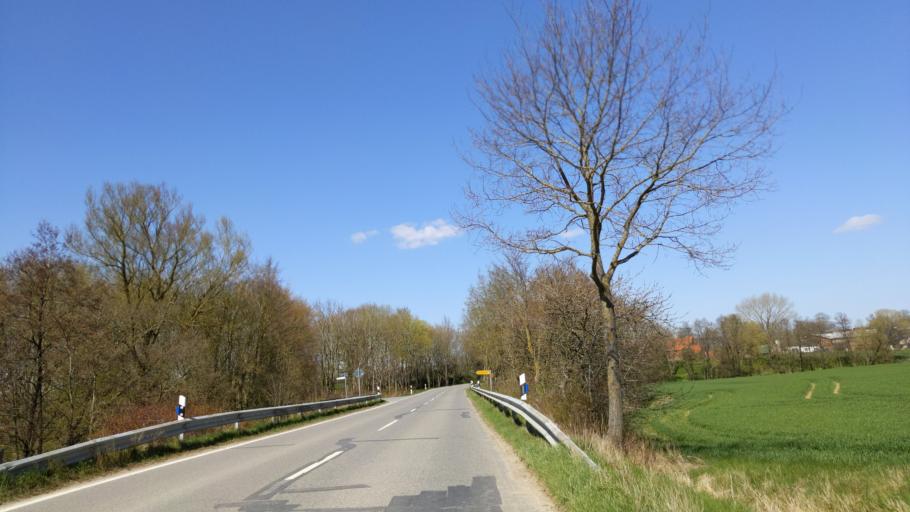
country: DE
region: Schleswig-Holstein
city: Susel
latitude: 54.0238
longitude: 10.6586
